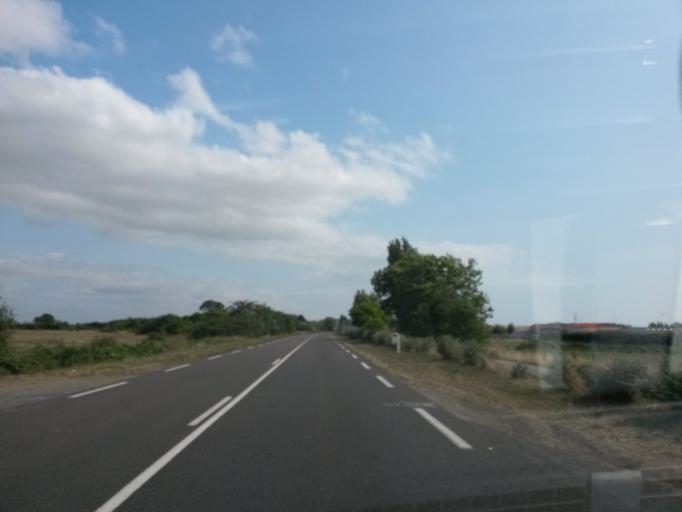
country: FR
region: Pays de la Loire
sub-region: Departement de la Vendee
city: La Tranche-sur-Mer
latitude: 46.3548
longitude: -1.4367
